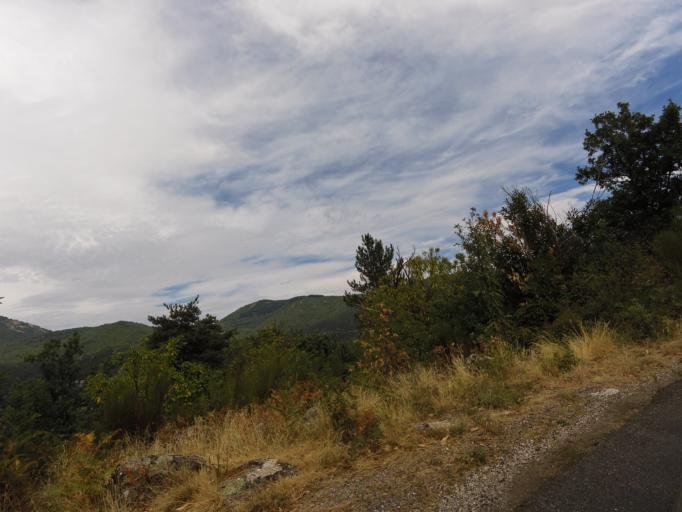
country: FR
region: Languedoc-Roussillon
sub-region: Departement du Gard
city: Le Vigan
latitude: 44.0200
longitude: 3.6328
